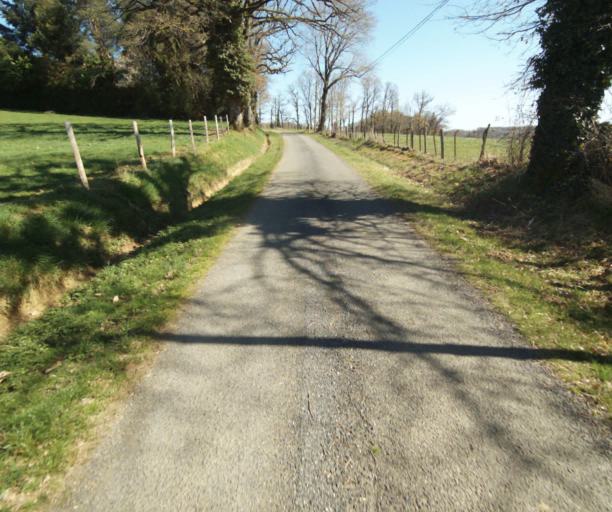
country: FR
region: Limousin
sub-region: Departement de la Correze
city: Chamboulive
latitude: 45.4015
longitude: 1.6498
